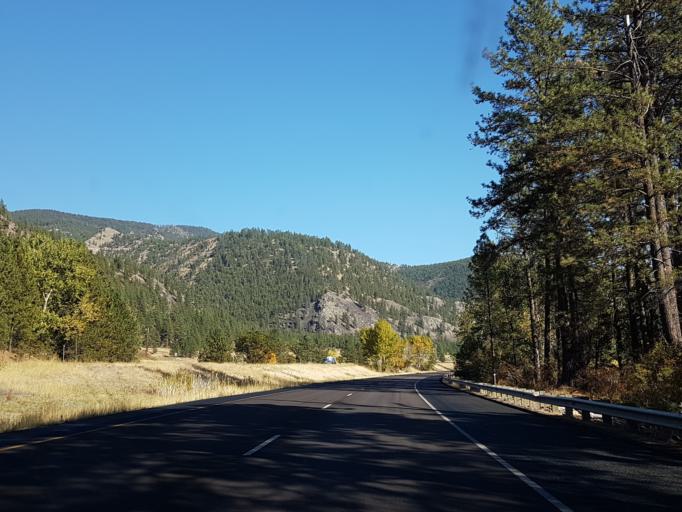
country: US
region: Montana
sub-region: Missoula County
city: Frenchtown
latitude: 47.0206
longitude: -114.5247
